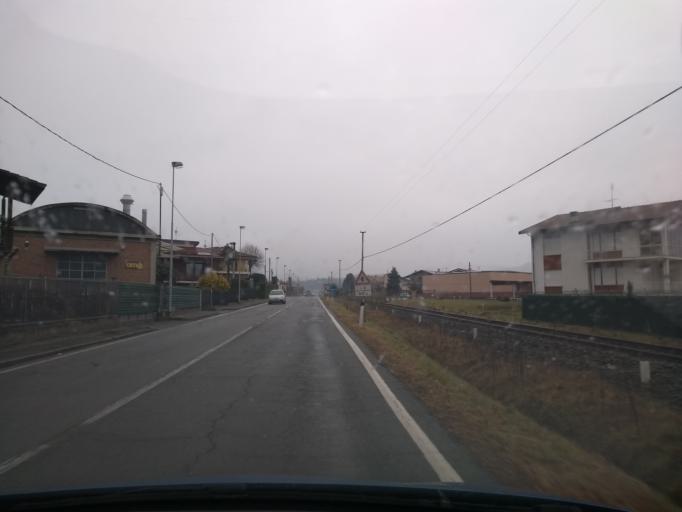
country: IT
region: Piedmont
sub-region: Provincia di Torino
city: Valperga
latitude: 45.3761
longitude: 7.6585
